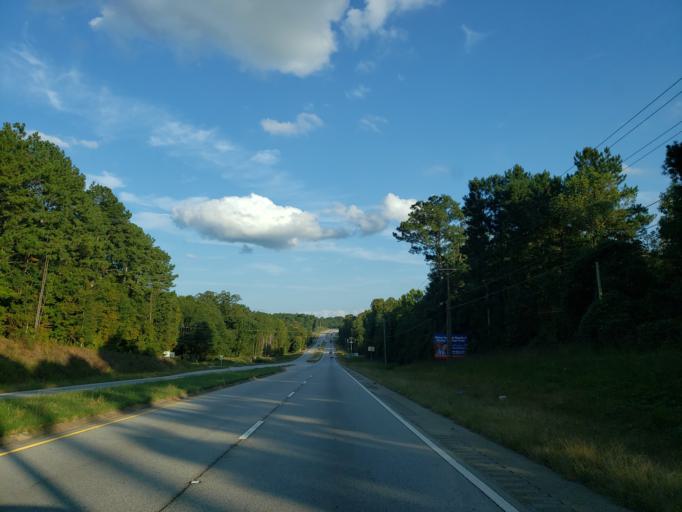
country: US
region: Georgia
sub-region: Carroll County
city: Carrollton
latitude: 33.6284
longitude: -85.1113
